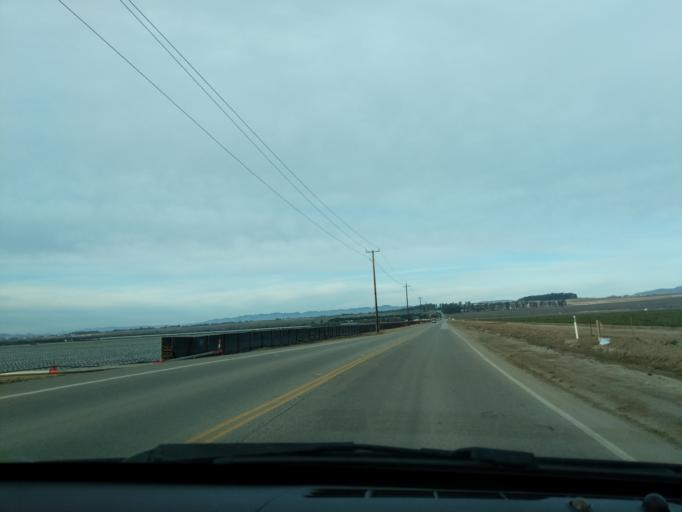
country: US
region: California
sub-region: Santa Barbara County
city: Guadalupe
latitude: 35.0040
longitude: -120.5704
